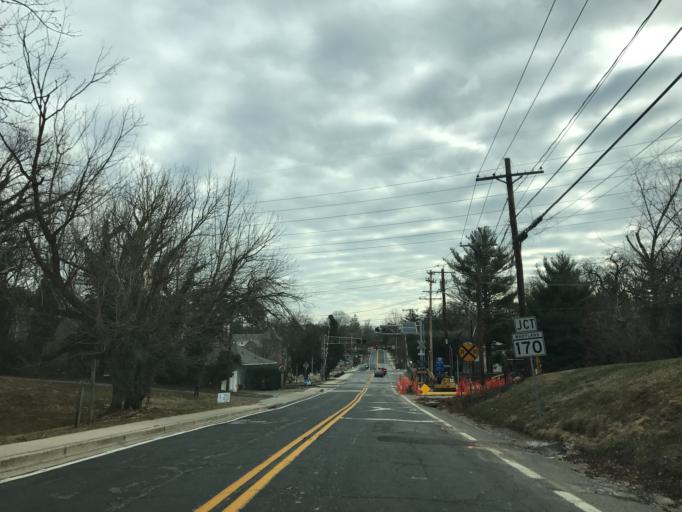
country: US
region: Maryland
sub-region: Anne Arundel County
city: Linthicum
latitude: 39.2054
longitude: -76.6544
